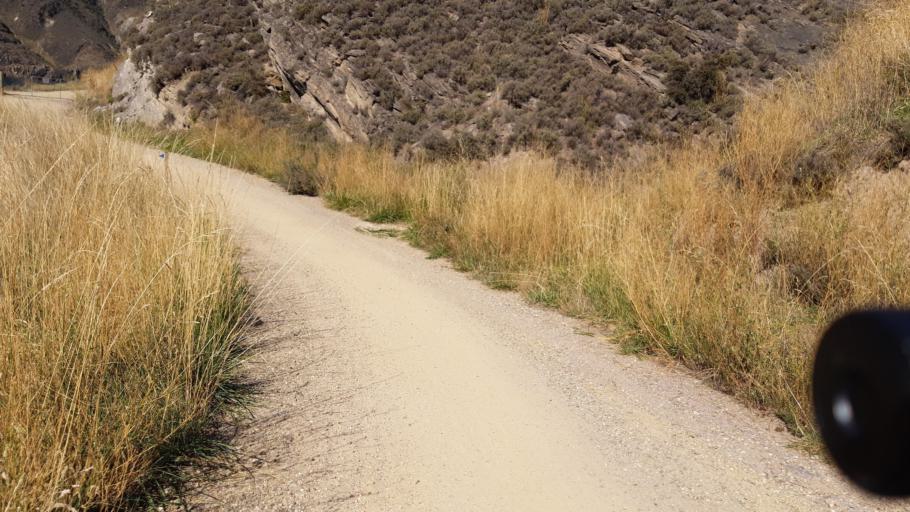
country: NZ
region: Otago
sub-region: Queenstown-Lakes District
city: Wanaka
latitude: -45.1311
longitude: 169.3099
